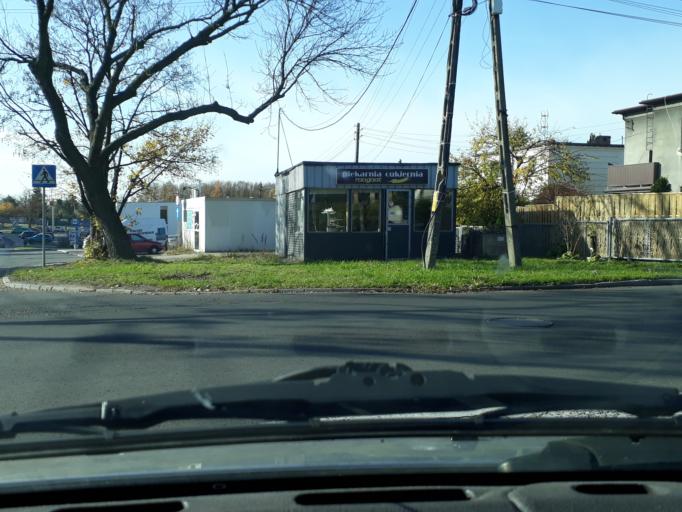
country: PL
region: Silesian Voivodeship
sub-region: Powiat tarnogorski
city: Tarnowskie Gory
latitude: 50.4343
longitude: 18.8675
